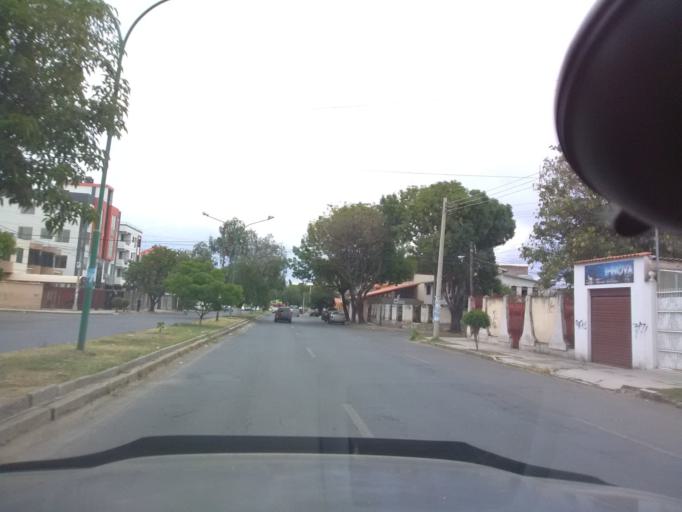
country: BO
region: Cochabamba
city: Cochabamba
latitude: -17.3828
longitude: -66.1676
